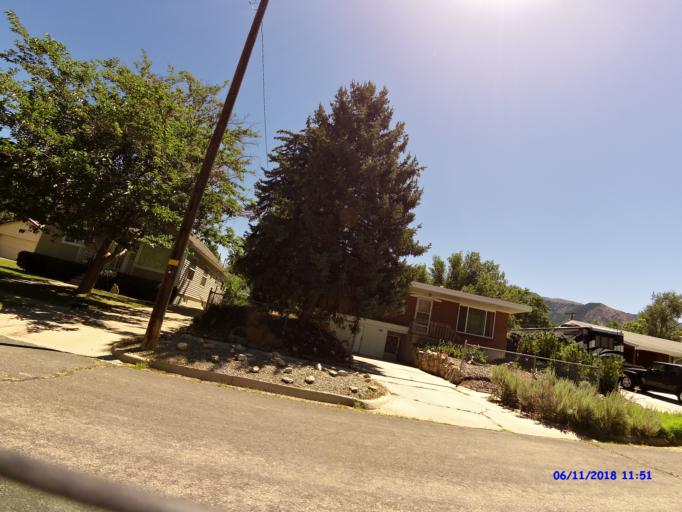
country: US
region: Utah
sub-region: Weber County
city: Ogden
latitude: 41.2335
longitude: -111.9521
